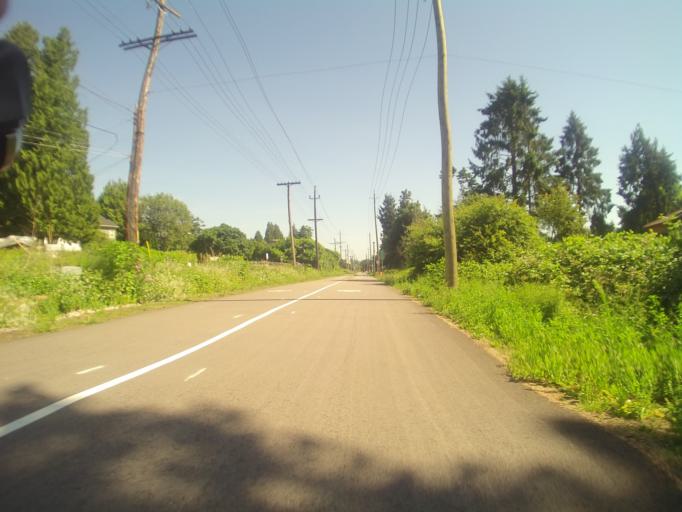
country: CA
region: British Columbia
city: Richmond
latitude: 49.2113
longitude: -123.1459
